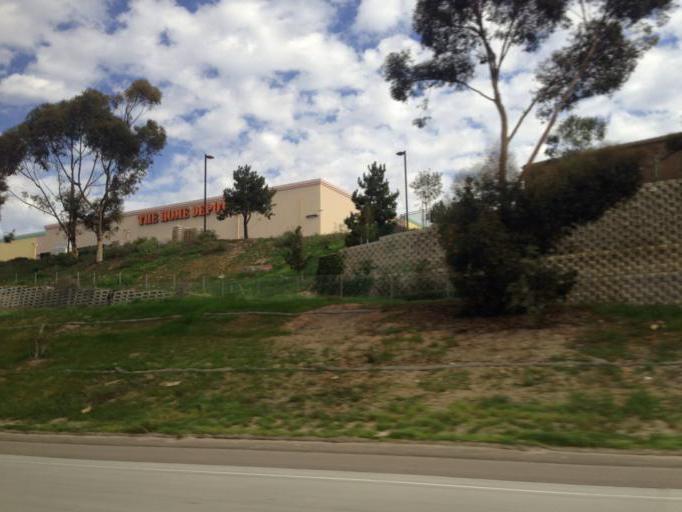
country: US
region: California
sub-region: San Diego County
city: Imperial Beach
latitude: 32.5755
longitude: -117.0387
